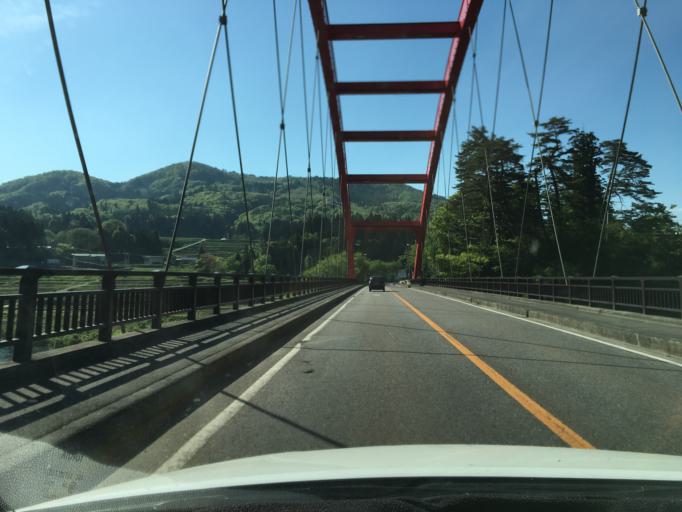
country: JP
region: Fukushima
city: Kitakata
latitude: 37.5308
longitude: 139.7236
